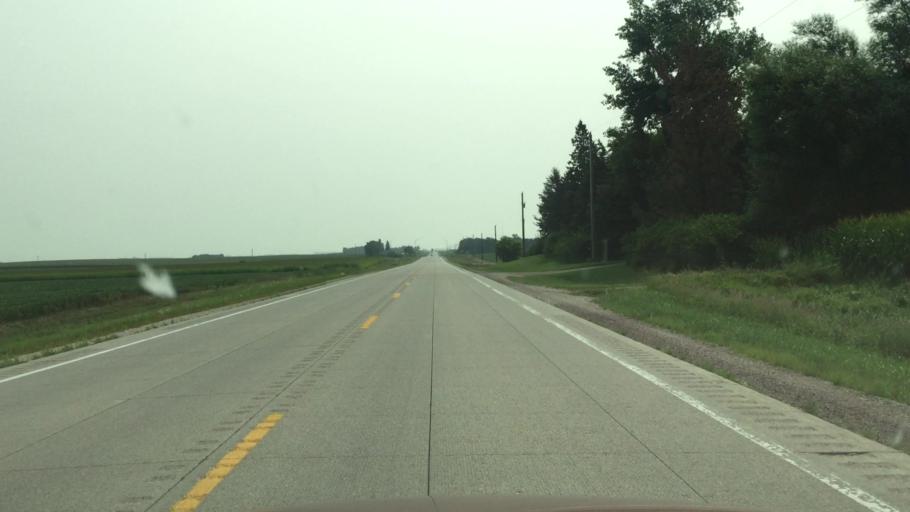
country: US
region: Iowa
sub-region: Osceola County
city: Sibley
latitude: 43.4327
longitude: -95.6505
